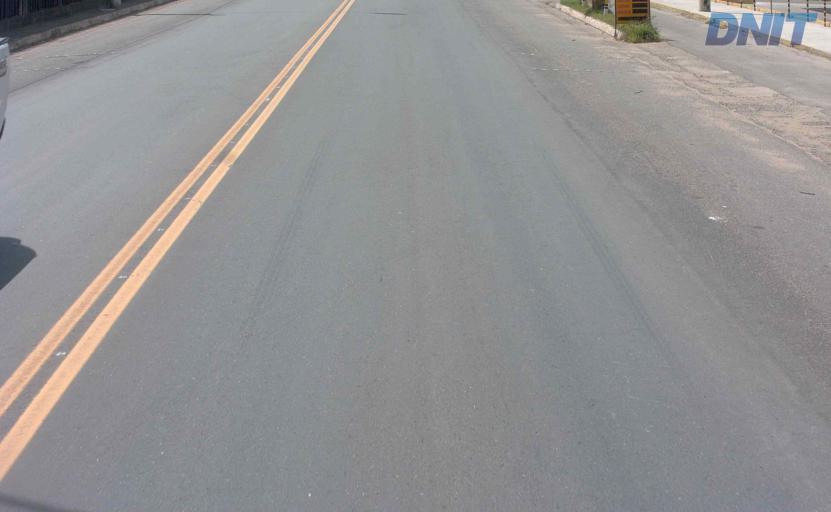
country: BR
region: Minas Gerais
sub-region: Governador Valadares
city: Governador Valadares
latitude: -18.8947
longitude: -41.9798
